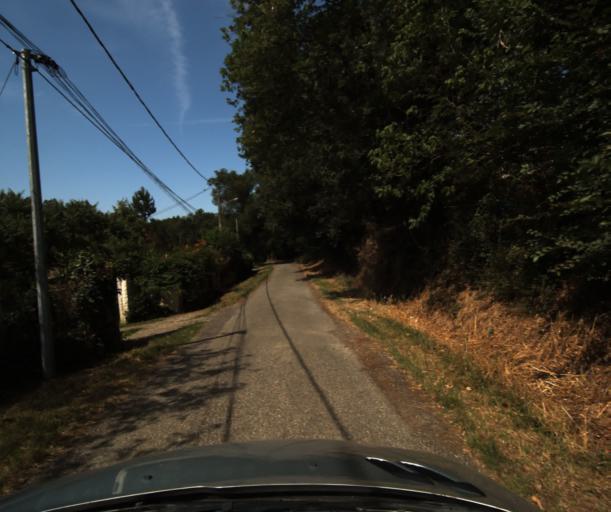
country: FR
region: Midi-Pyrenees
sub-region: Departement de la Haute-Garonne
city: Lherm
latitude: 43.4602
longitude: 1.2124
